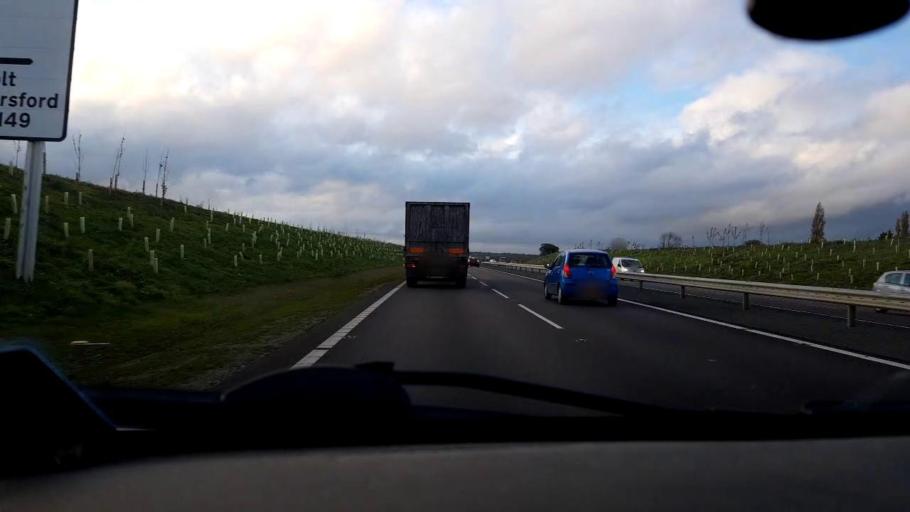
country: GB
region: England
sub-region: Norfolk
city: Horsford
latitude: 52.6849
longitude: 1.2458
